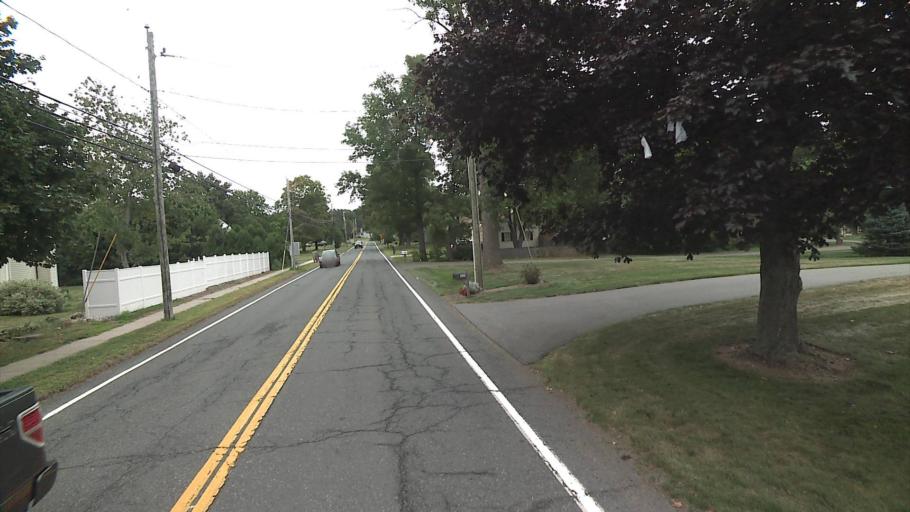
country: US
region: Connecticut
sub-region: Hartford County
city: Manchester
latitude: 41.8024
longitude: -72.4712
